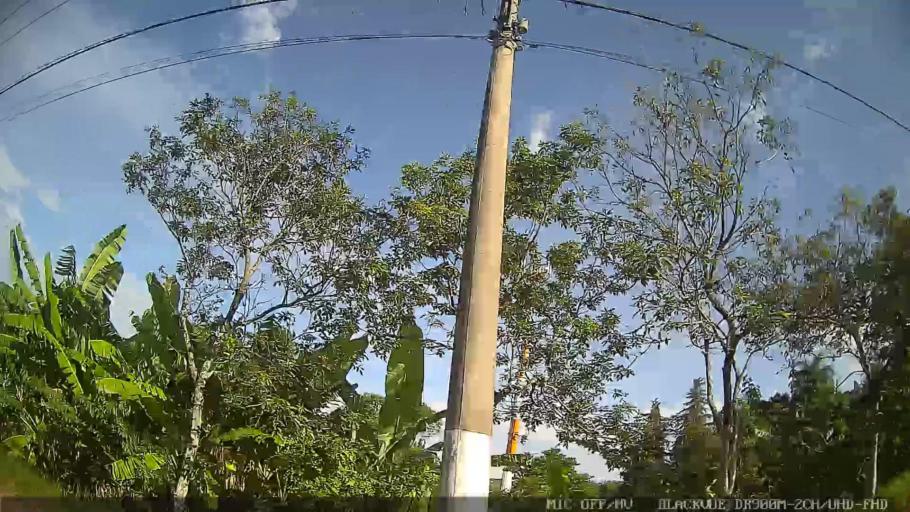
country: BR
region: Sao Paulo
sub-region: Serra Negra
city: Serra Negra
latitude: -22.6174
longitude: -46.7045
